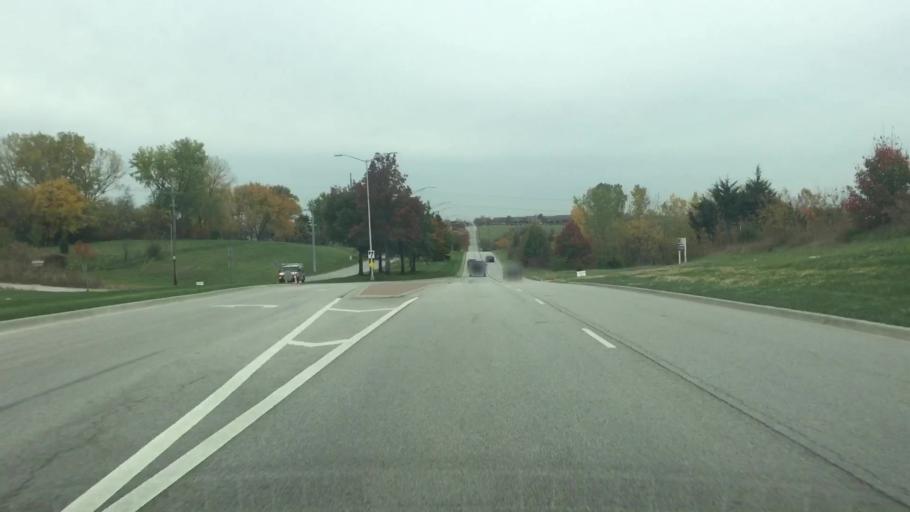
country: US
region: Kansas
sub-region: Johnson County
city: Lenexa
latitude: 38.9379
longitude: -94.7796
